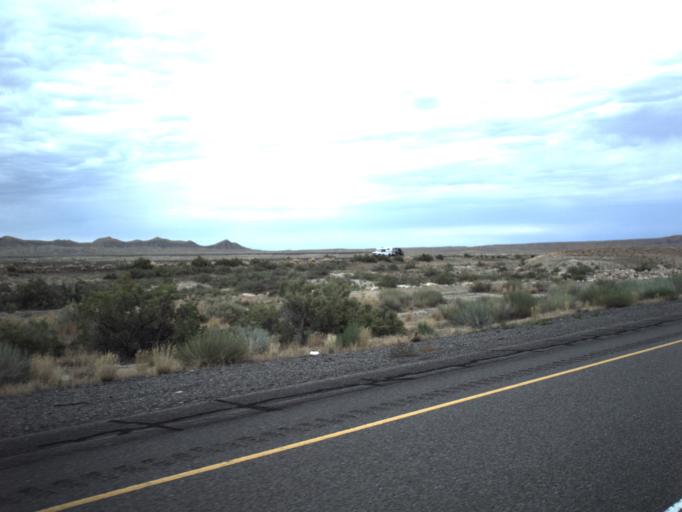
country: US
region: Utah
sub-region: Grand County
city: Moab
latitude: 38.9401
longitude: -109.5168
